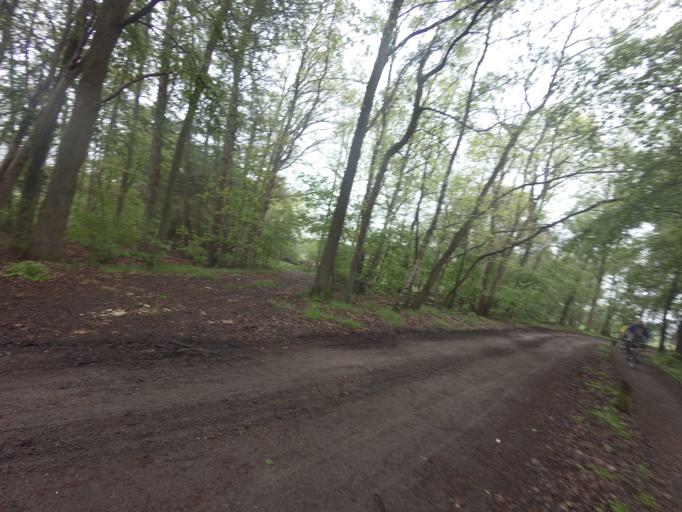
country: DE
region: North Rhine-Westphalia
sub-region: Regierungsbezirk Munster
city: Vreden
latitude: 52.1272
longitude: 6.8495
